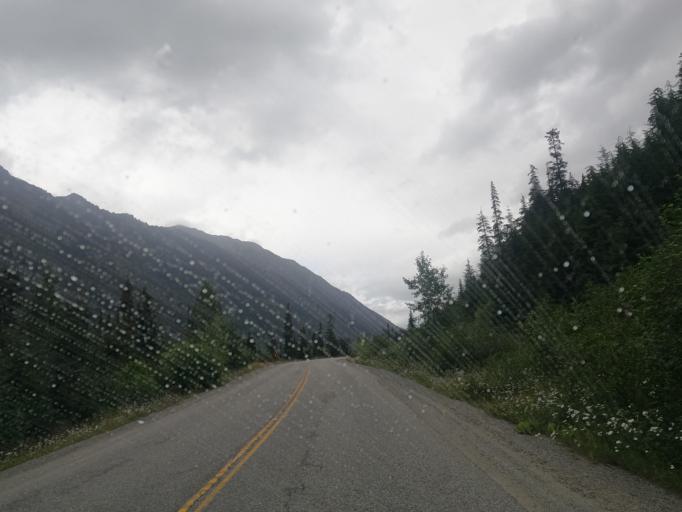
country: CA
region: British Columbia
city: Lillooet
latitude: 50.4026
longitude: -122.3079
